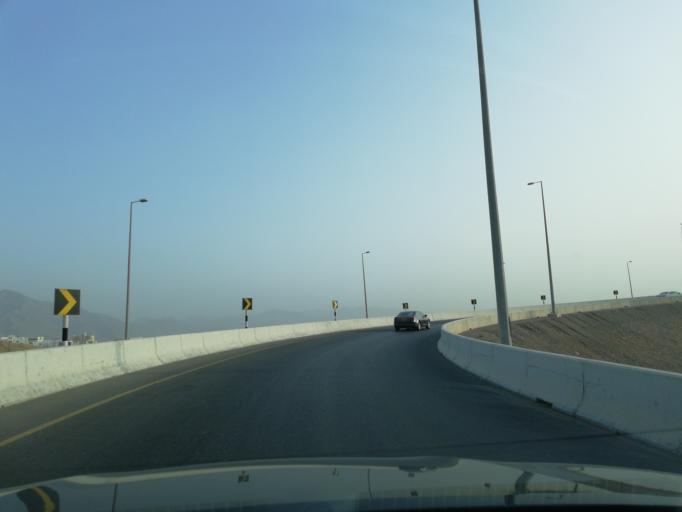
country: OM
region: Muhafazat Masqat
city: Bawshar
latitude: 23.5654
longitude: 58.3802
